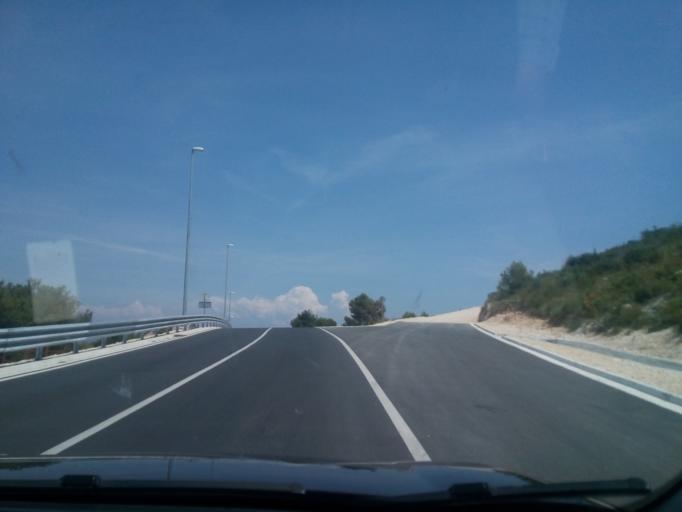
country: HR
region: Splitsko-Dalmatinska
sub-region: Grad Trogir
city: Trogir
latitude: 43.5158
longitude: 16.2684
